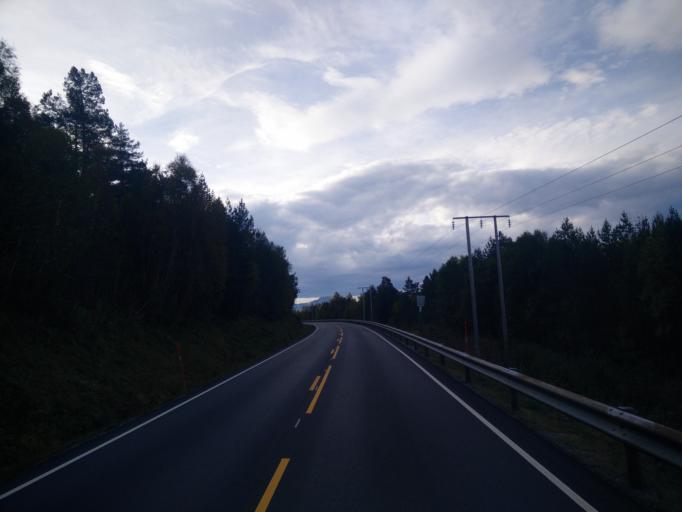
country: NO
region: More og Romsdal
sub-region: Gjemnes
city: Batnfjordsora
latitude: 62.8445
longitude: 7.5982
